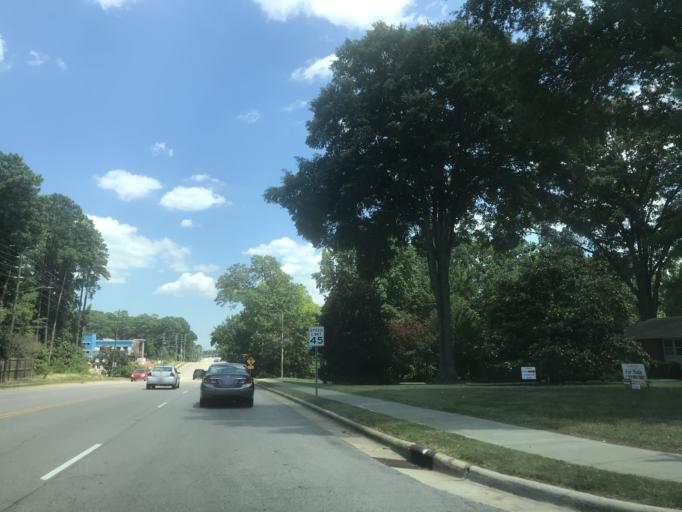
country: US
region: North Carolina
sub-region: Wake County
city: Cary
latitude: 35.7659
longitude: -78.7554
